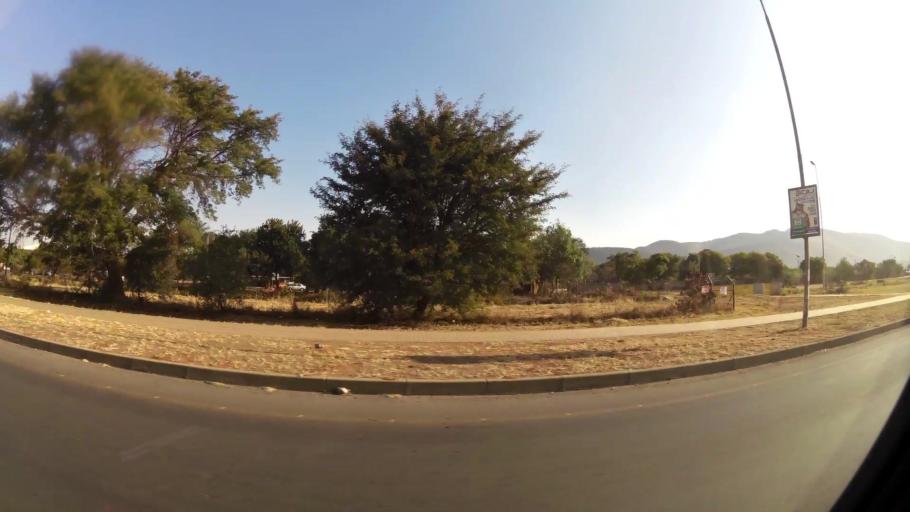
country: ZA
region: North-West
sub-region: Bojanala Platinum District Municipality
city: Rustenburg
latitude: -25.6518
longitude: 27.2171
